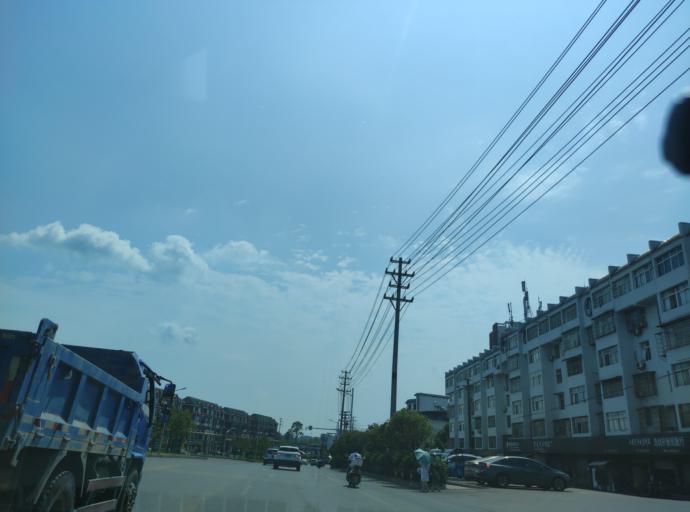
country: CN
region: Jiangxi Sheng
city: Pingxiang
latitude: 27.6589
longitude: 113.8992
